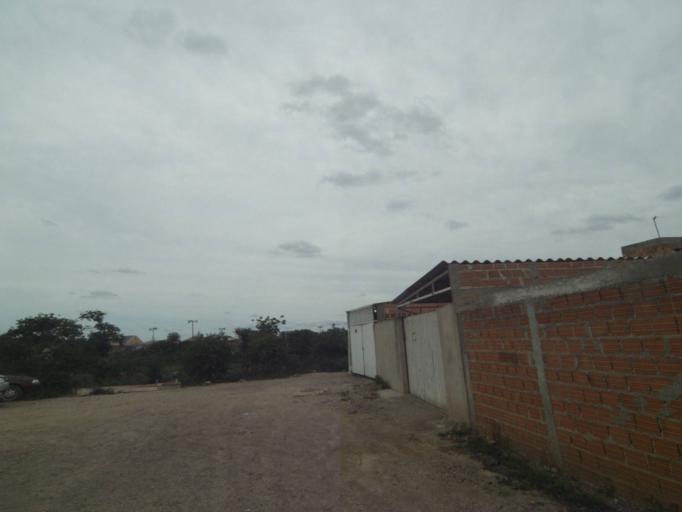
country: BR
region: Parana
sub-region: Curitiba
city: Curitiba
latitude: -25.5088
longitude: -49.3380
